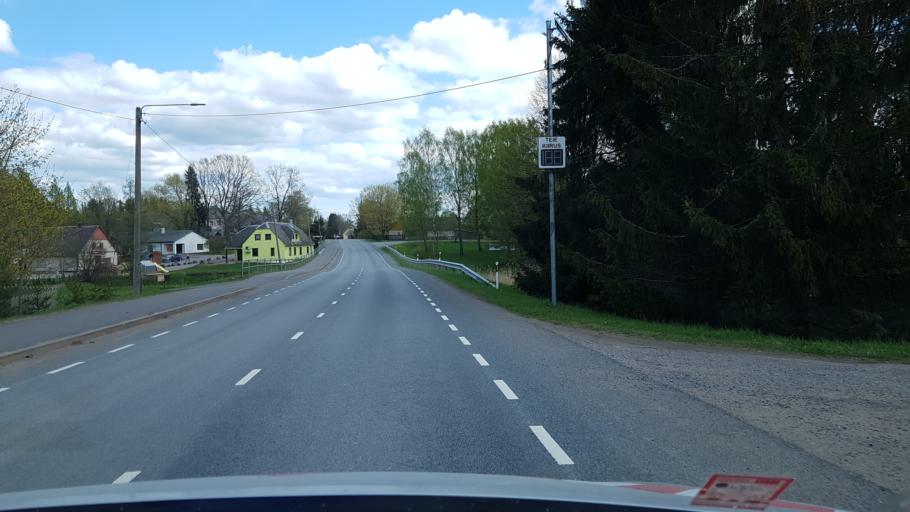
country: EE
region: Polvamaa
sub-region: Polva linn
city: Polva
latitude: 58.2843
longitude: 27.0428
